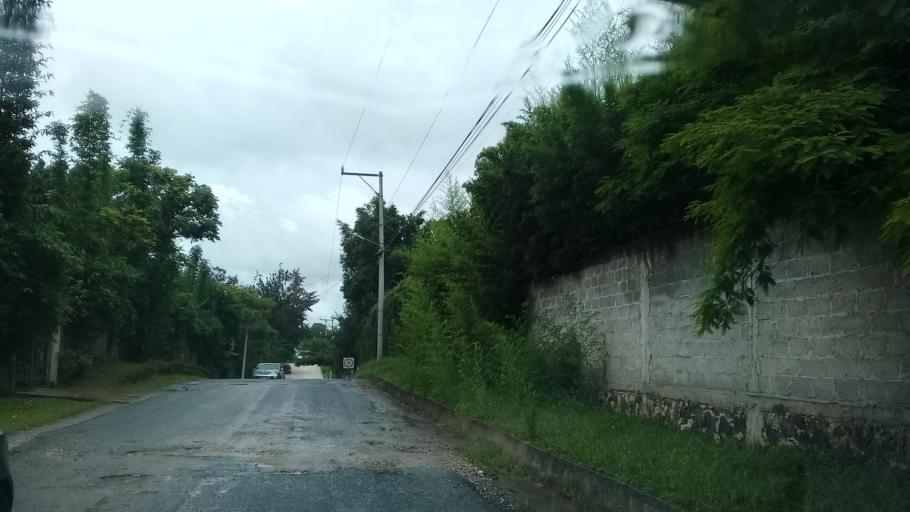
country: MX
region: Veracruz
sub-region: Emiliano Zapata
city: Jacarandas
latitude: 19.5046
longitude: -96.8435
